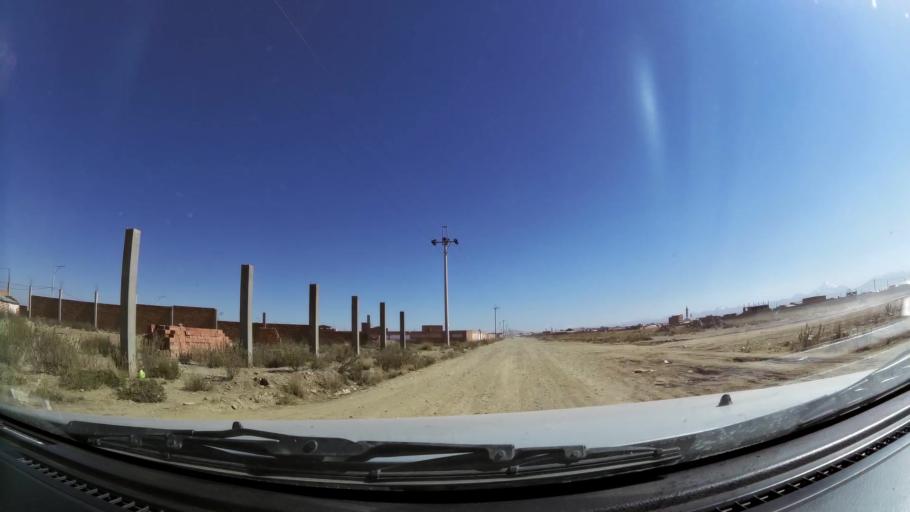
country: BO
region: La Paz
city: La Paz
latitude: -16.5811
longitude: -68.2152
